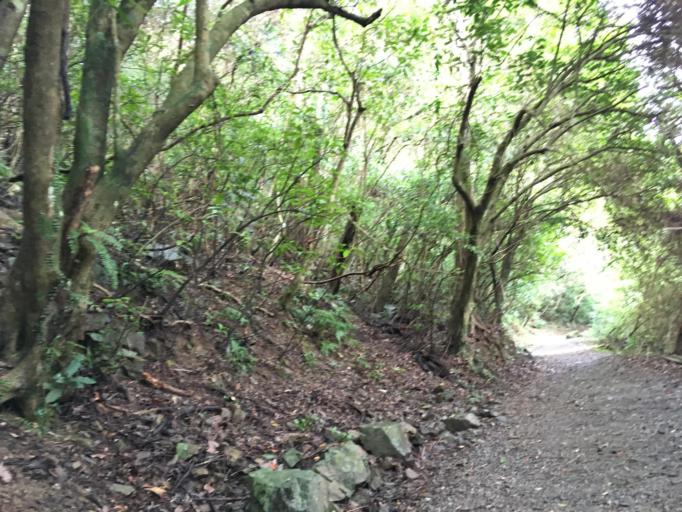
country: TW
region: Taiwan
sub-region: Yilan
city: Yilan
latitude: 24.8388
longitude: 121.7736
